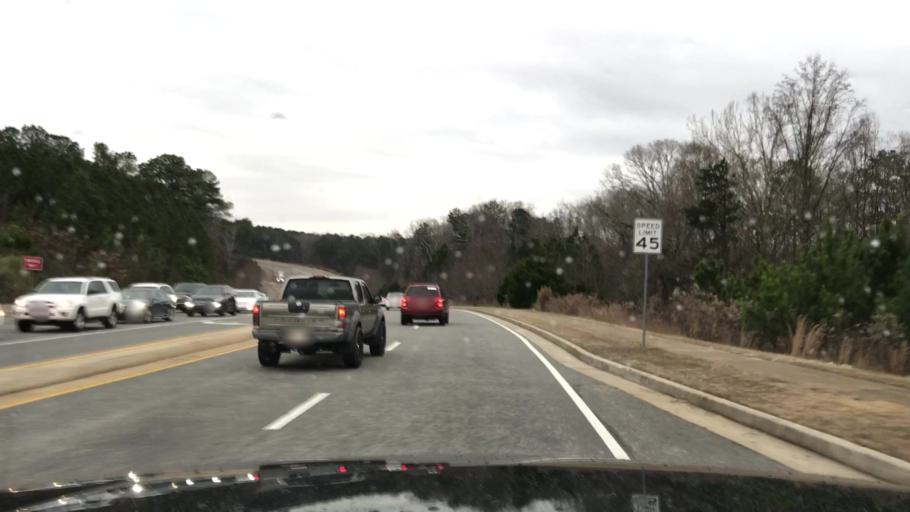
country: US
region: Georgia
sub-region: Gwinnett County
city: Suwanee
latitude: 34.0227
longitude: -84.0516
